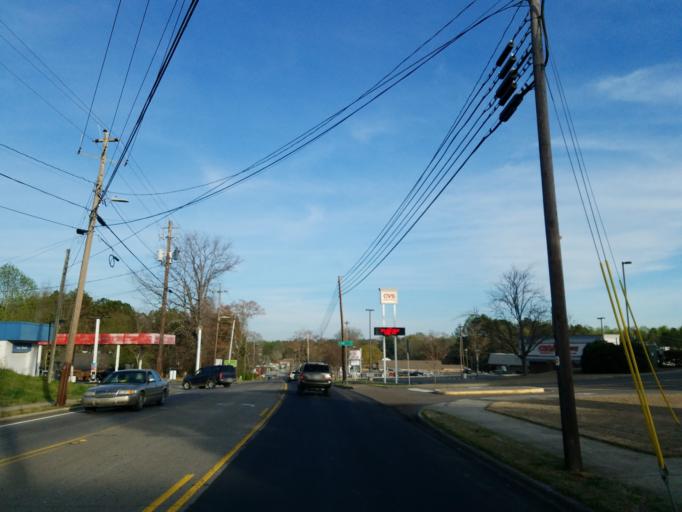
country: US
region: Georgia
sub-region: Pickens County
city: Jasper
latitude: 34.4682
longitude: -84.4266
